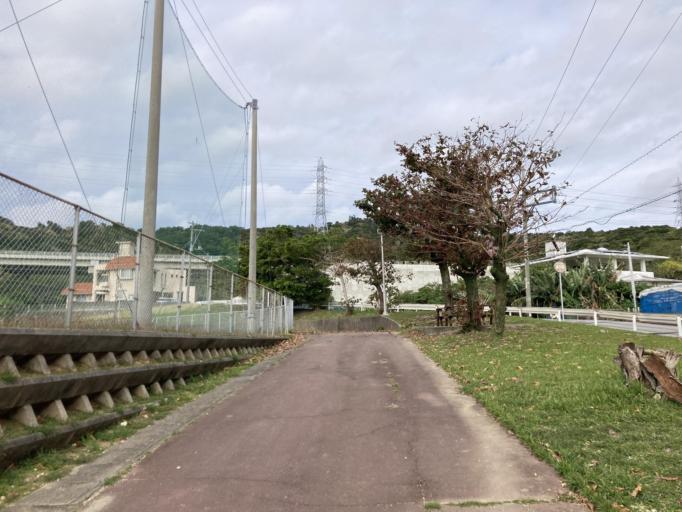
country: JP
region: Okinawa
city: Ginowan
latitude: 26.2081
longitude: 127.7546
